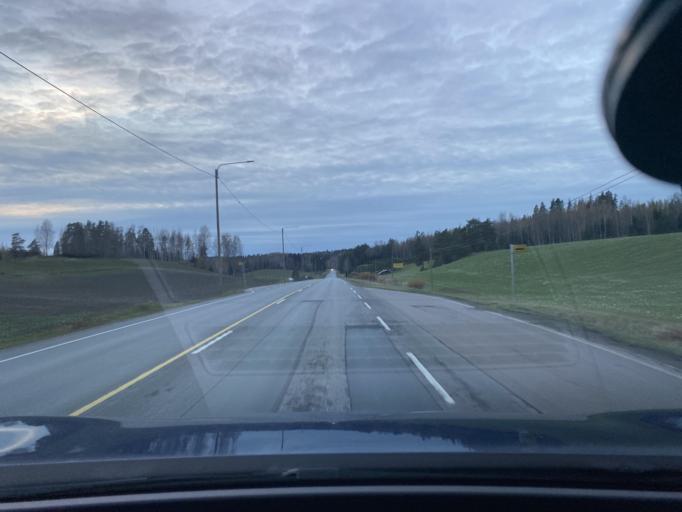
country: FI
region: Uusimaa
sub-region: Helsinki
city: Saukkola
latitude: 60.3879
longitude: 24.0488
